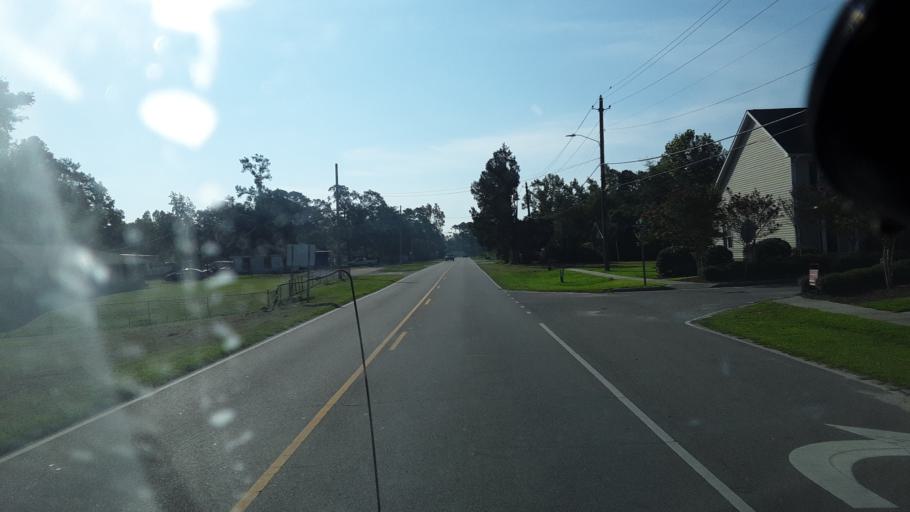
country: US
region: North Carolina
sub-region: Brunswick County
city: Leland
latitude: 34.2553
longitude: -78.0428
